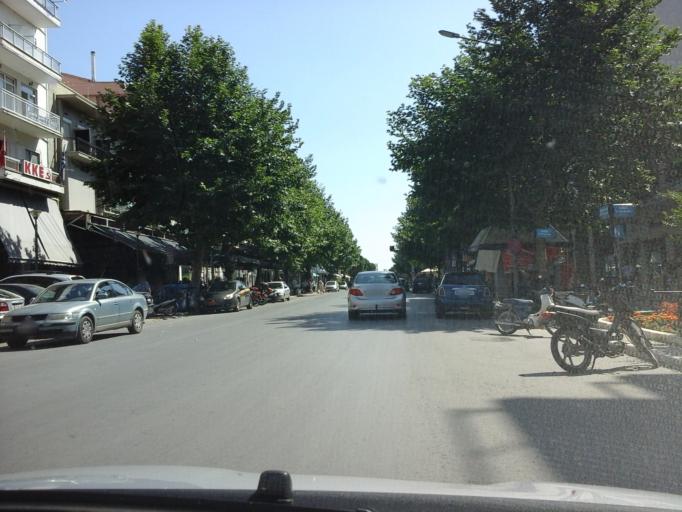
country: GR
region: East Macedonia and Thrace
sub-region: Nomos Evrou
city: Alexandroupoli
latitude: 40.8450
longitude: 25.8746
